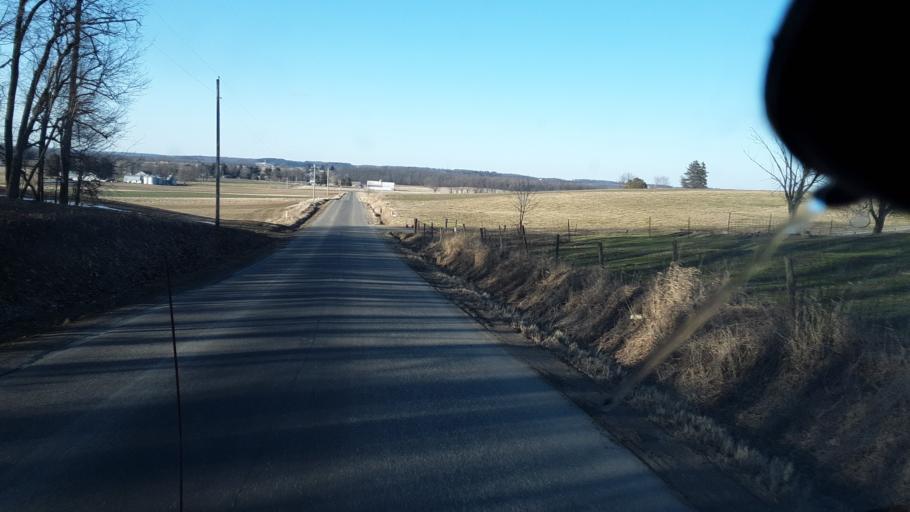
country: US
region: Ohio
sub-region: Wayne County
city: Apple Creek
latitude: 40.7195
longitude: -81.8427
